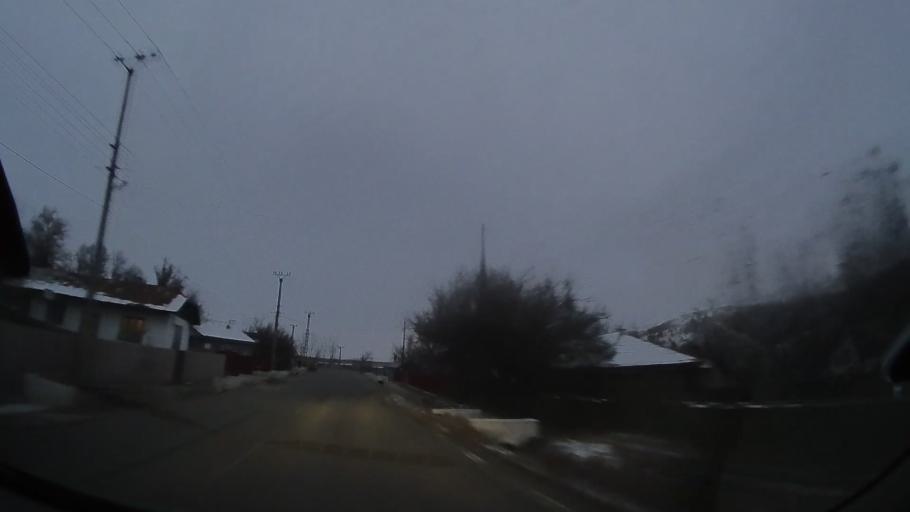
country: RO
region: Vaslui
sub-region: Comuna Vutcani
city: Vutcani
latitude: 46.4151
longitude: 27.9971
